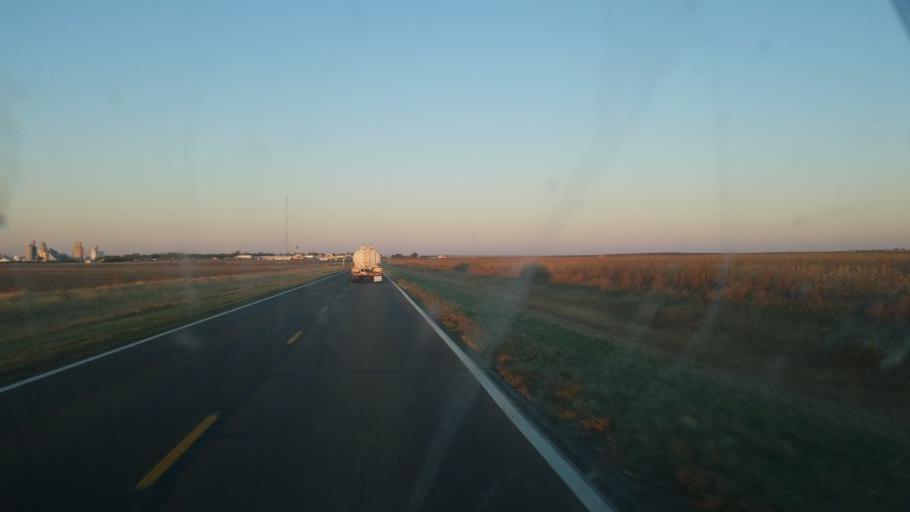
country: US
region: Kansas
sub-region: Wallace County
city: Sharon Springs
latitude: 38.9020
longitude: -101.7261
